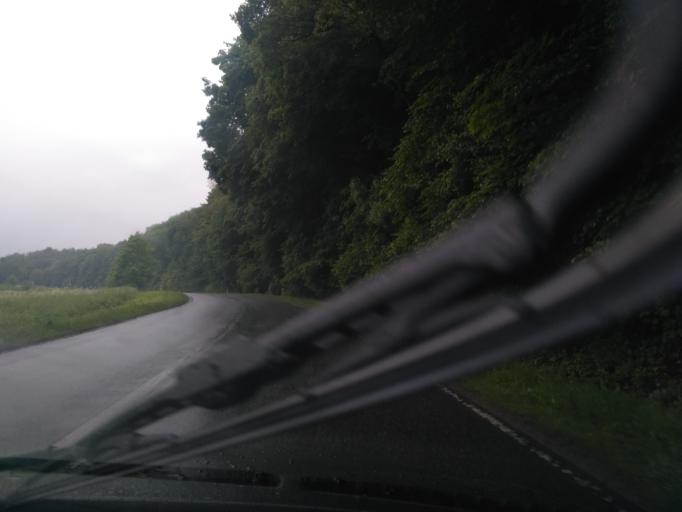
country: PL
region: Subcarpathian Voivodeship
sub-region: Powiat krosnienski
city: Leki
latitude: 49.8159
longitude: 21.6338
